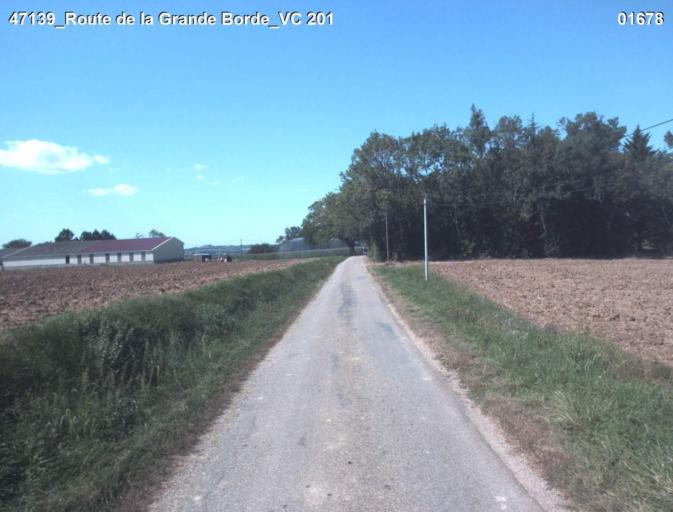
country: FR
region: Aquitaine
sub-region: Departement du Lot-et-Garonne
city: Nerac
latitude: 44.0745
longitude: 0.3843
